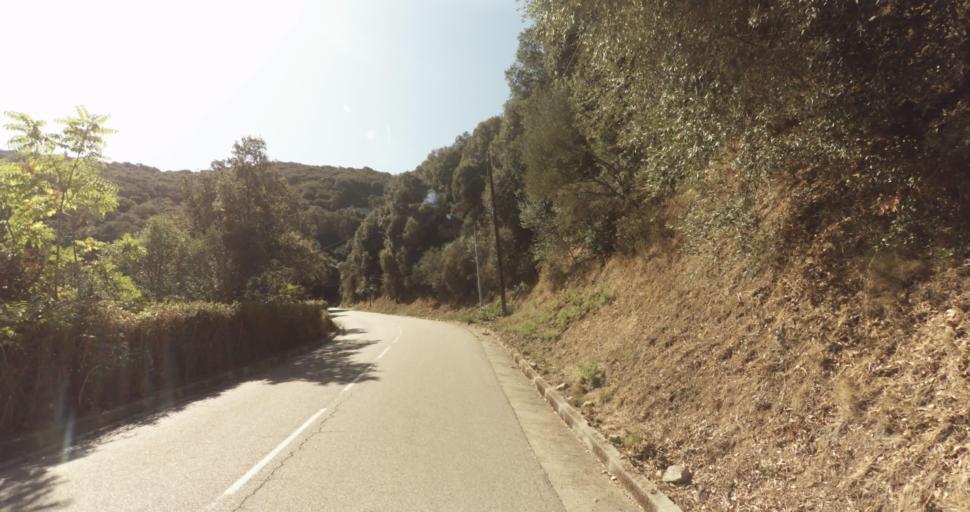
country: FR
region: Corsica
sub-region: Departement de la Corse-du-Sud
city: Ajaccio
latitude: 41.9257
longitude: 8.7085
